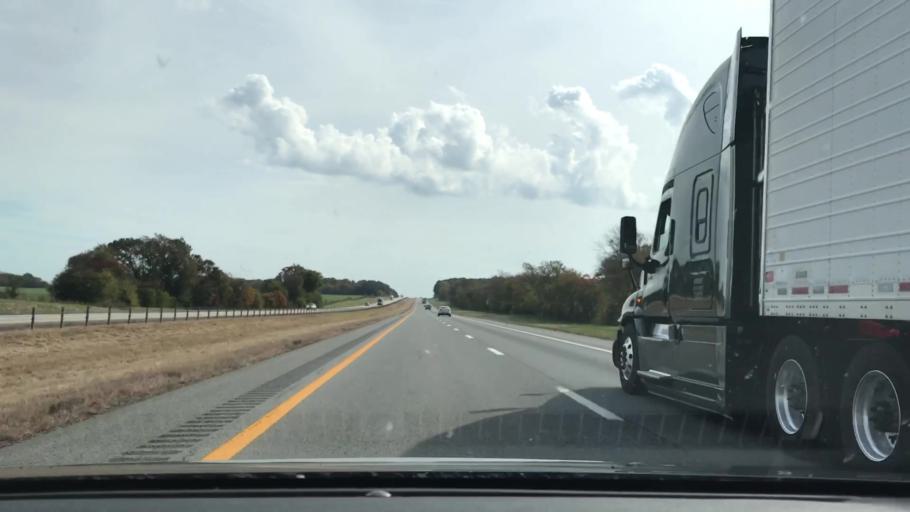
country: US
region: Kentucky
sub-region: Christian County
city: Hopkinsville
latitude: 36.7848
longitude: -87.5807
